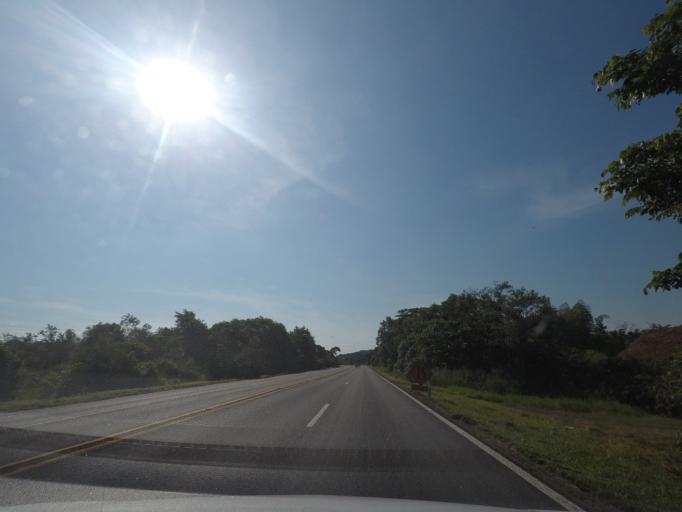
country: BR
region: Parana
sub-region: Paranagua
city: Paranagua
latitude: -25.5770
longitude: -48.6127
